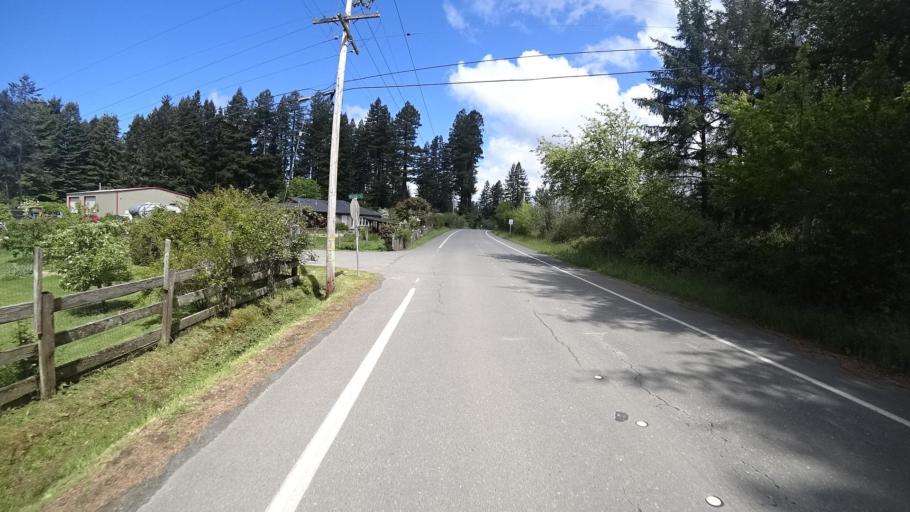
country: US
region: California
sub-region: Humboldt County
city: McKinleyville
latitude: 40.9532
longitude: -124.0334
